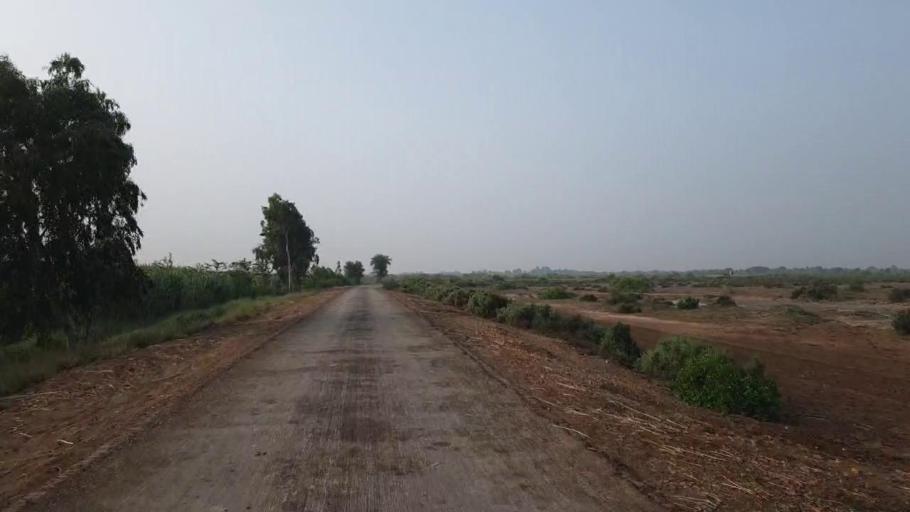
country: PK
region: Sindh
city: Tando Muhammad Khan
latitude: 25.1537
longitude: 68.6087
